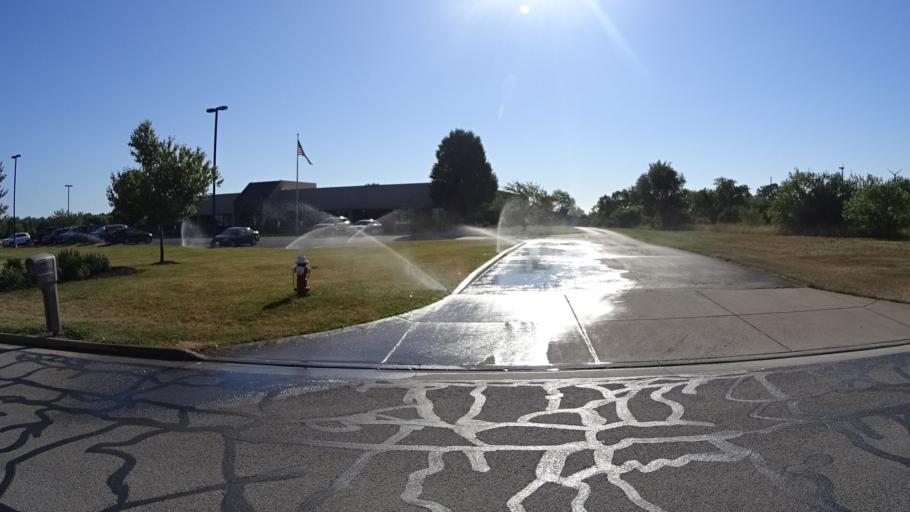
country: US
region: Ohio
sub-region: Erie County
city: Sandusky
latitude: 41.4128
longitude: -82.7614
